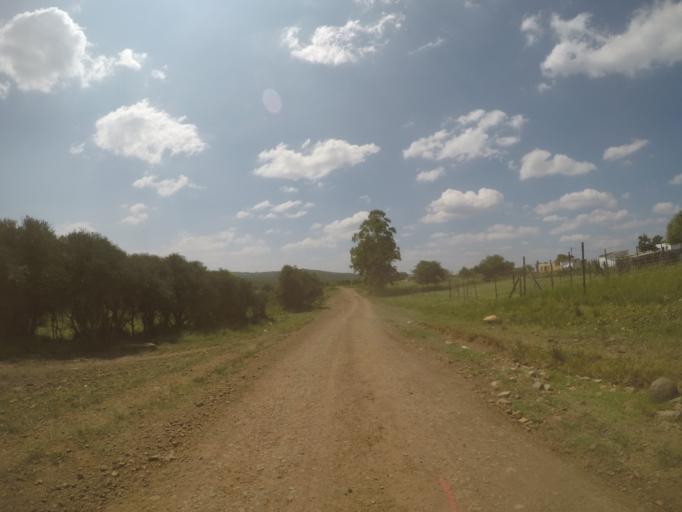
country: ZA
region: KwaZulu-Natal
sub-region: uThungulu District Municipality
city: Empangeni
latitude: -28.5903
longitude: 31.7366
